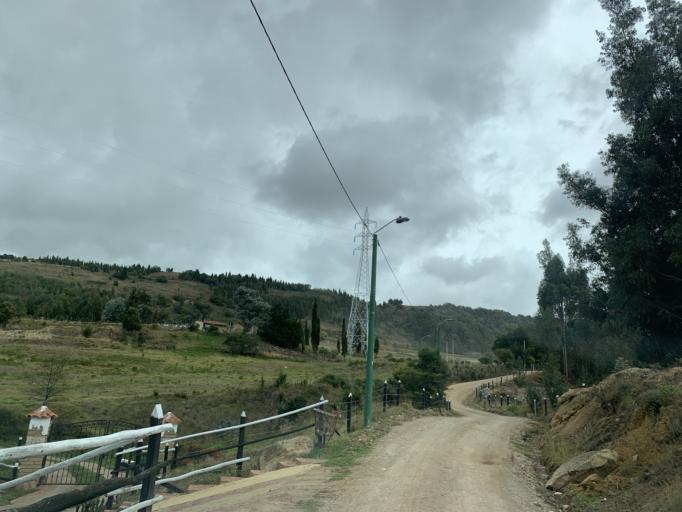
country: CO
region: Boyaca
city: Tunja
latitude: 5.5638
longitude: -73.3207
